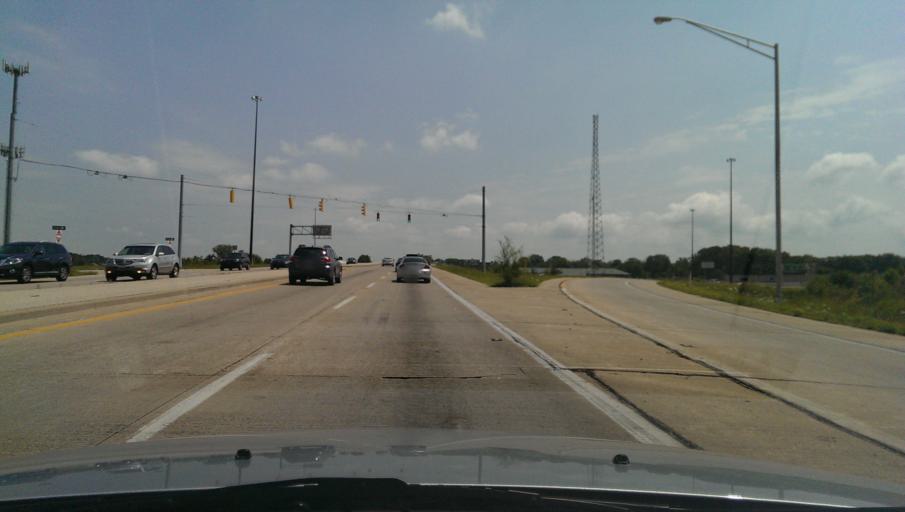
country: US
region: Indiana
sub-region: Marion County
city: Lawrence
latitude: 39.8550
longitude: -86.0500
